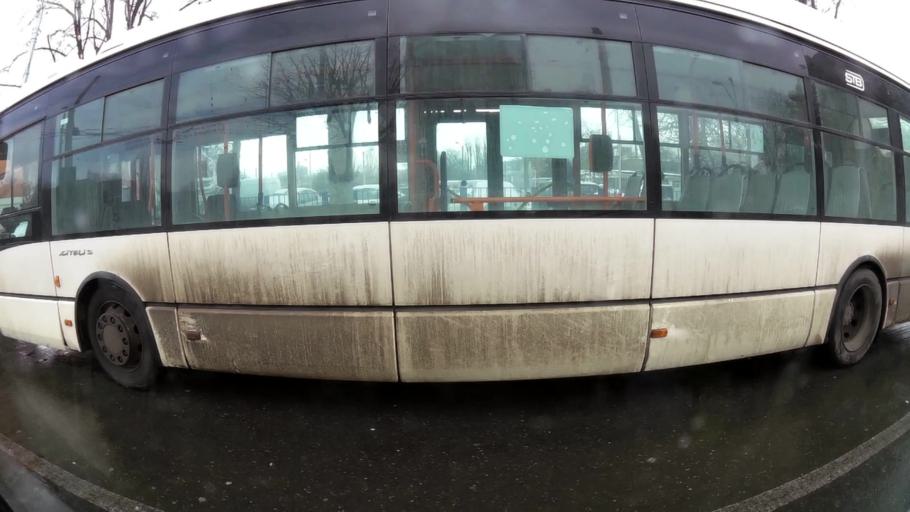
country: RO
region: Bucuresti
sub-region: Municipiul Bucuresti
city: Bucuresti
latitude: 44.3889
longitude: 26.1186
